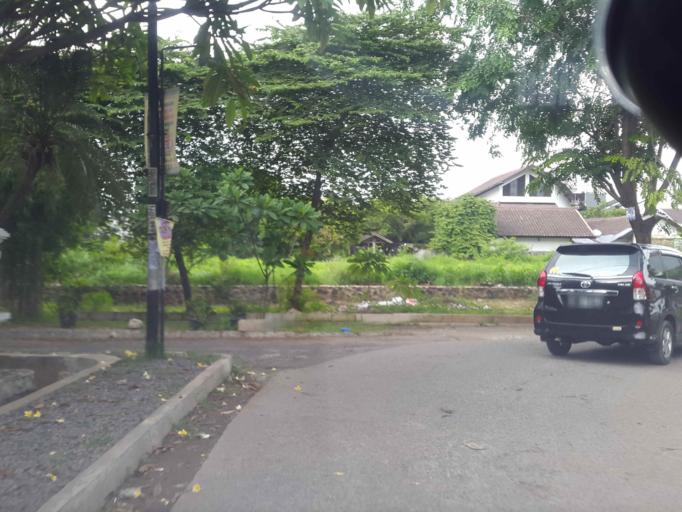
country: ID
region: West Java
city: Bekasi
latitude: -6.2700
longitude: 106.9232
